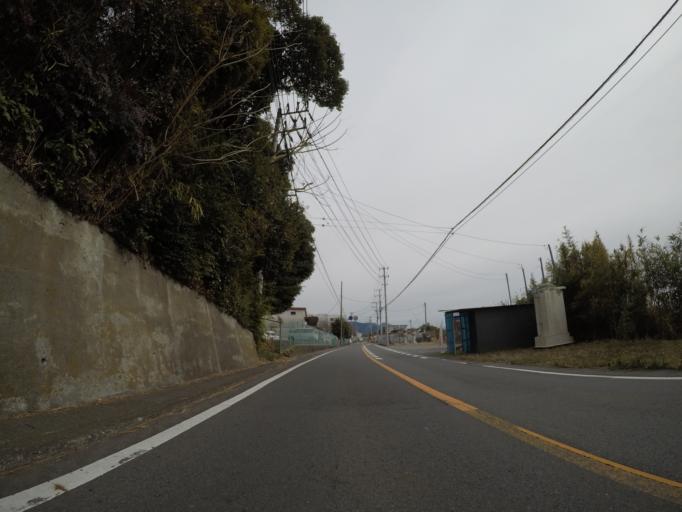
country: JP
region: Shizuoka
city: Fujinomiya
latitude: 35.2151
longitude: 138.6675
